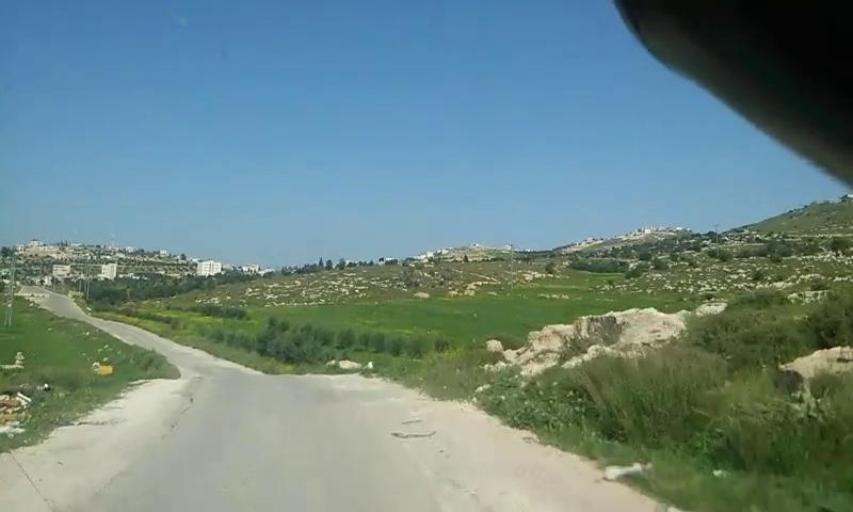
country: PS
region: West Bank
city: Al Majd
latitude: 31.4953
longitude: 34.9609
